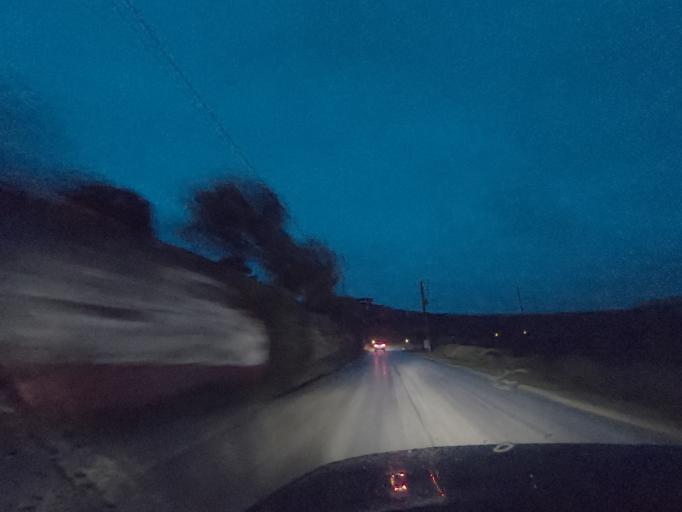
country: PT
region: Vila Real
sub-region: Sabrosa
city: Sabrosa
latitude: 41.2263
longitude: -7.5577
